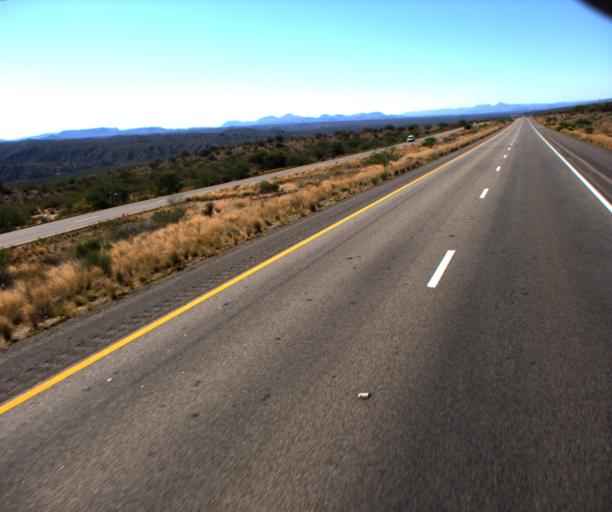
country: US
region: Arizona
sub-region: Mohave County
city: Kingman
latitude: 34.8785
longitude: -113.6477
